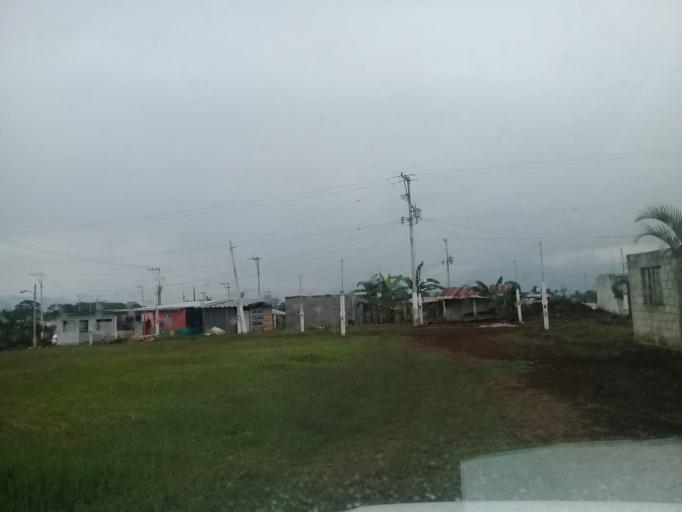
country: MX
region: Veracruz
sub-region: Cordoba
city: San Jose de Tapia
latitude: 18.8511
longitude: -96.9569
